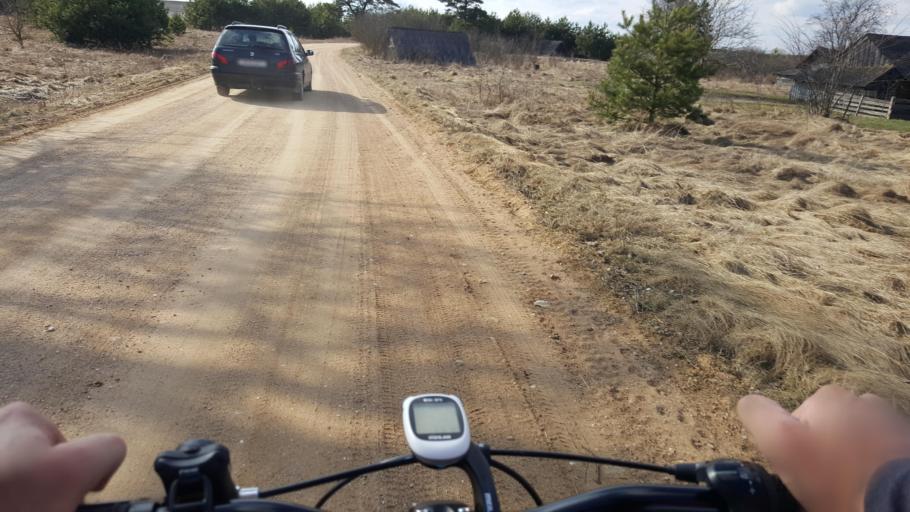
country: BY
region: Brest
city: Kamyanyets
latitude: 52.4135
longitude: 23.9333
